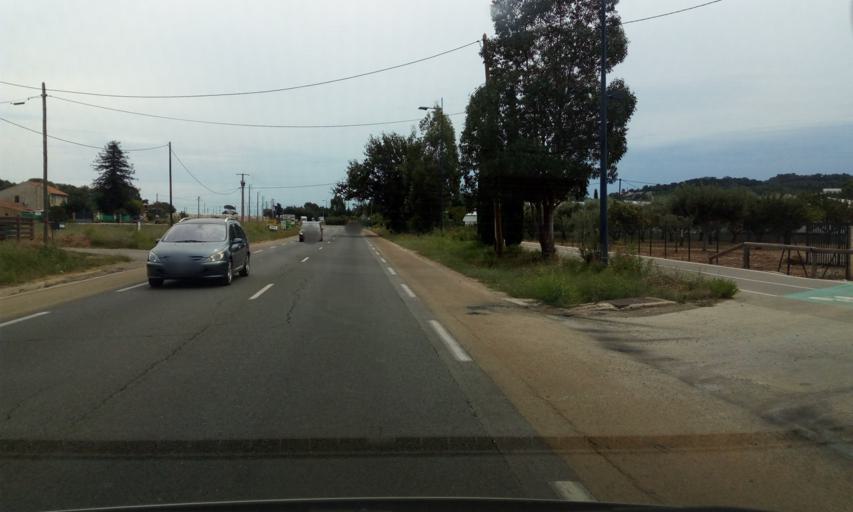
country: FR
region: Provence-Alpes-Cote d'Azur
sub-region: Departement du Var
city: Carqueiranne
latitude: 43.1051
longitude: 6.0534
